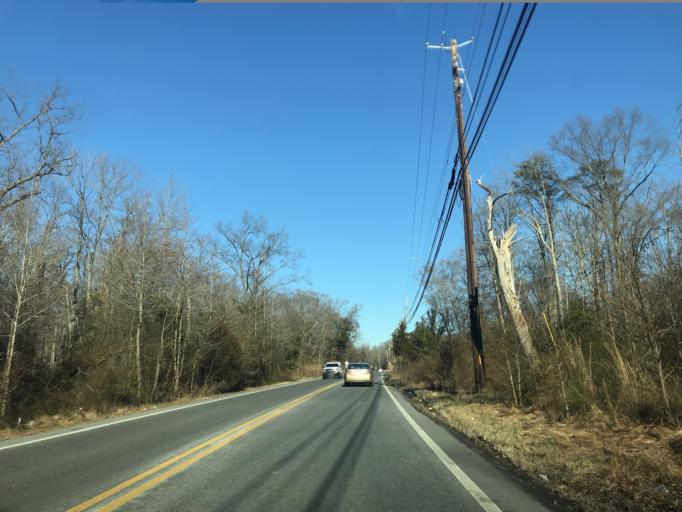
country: US
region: Maryland
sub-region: Prince George's County
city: Friendly
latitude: 38.7179
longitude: -76.9605
